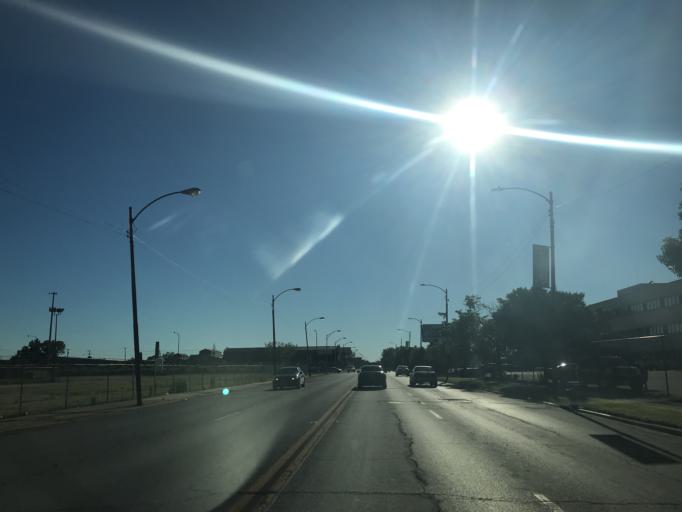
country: US
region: Illinois
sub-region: Cook County
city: Cicero
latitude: 41.8657
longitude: -87.7572
